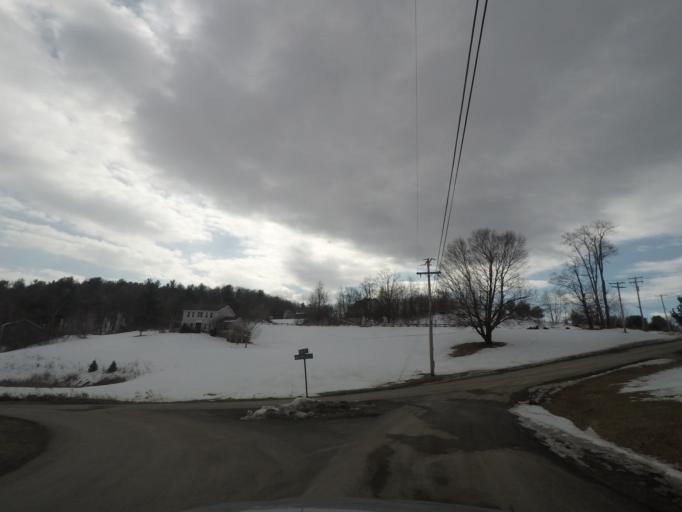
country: US
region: New York
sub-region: Saratoga County
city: Waterford
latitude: 42.7823
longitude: -73.6128
